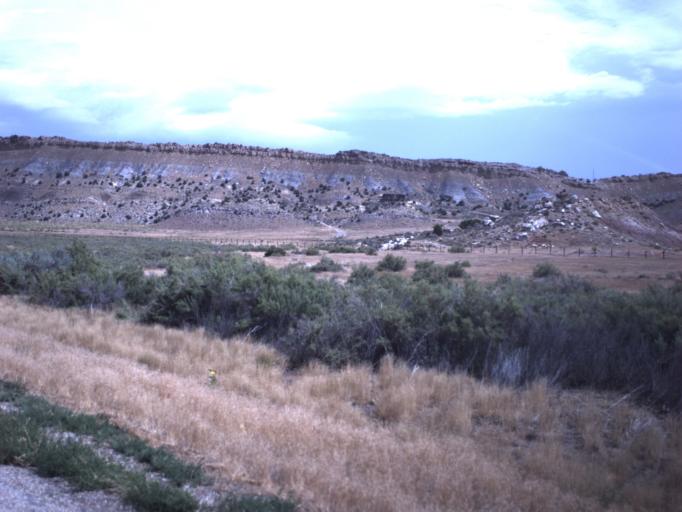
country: US
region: Utah
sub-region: Uintah County
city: Vernal
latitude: 40.5328
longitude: -109.5220
